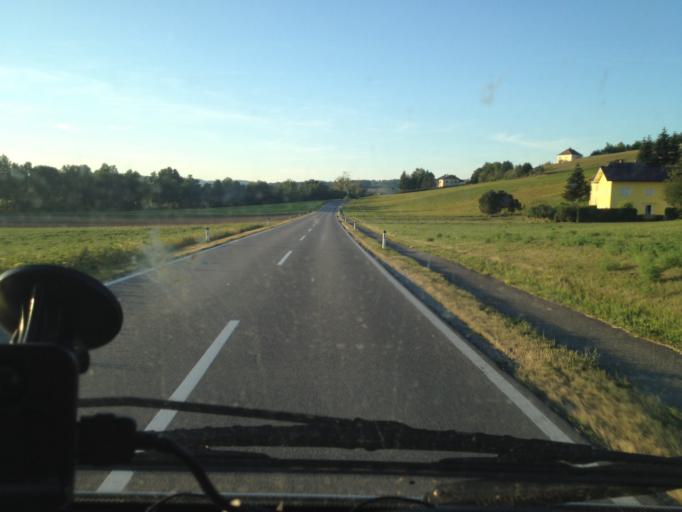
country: AT
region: Upper Austria
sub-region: Politischer Bezirk Urfahr-Umgebung
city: Engerwitzdorf
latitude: 48.3073
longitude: 14.4851
